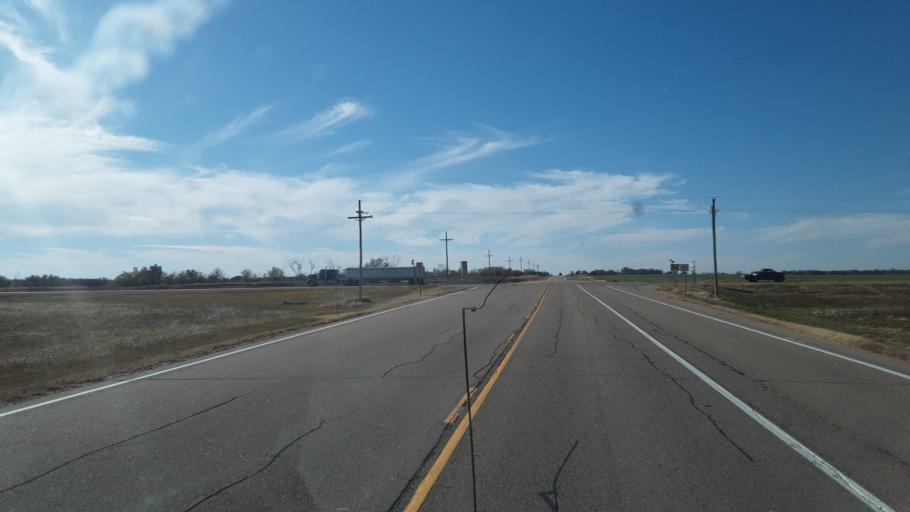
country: US
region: Kansas
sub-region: Pawnee County
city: Larned
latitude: 38.1895
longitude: -99.3128
